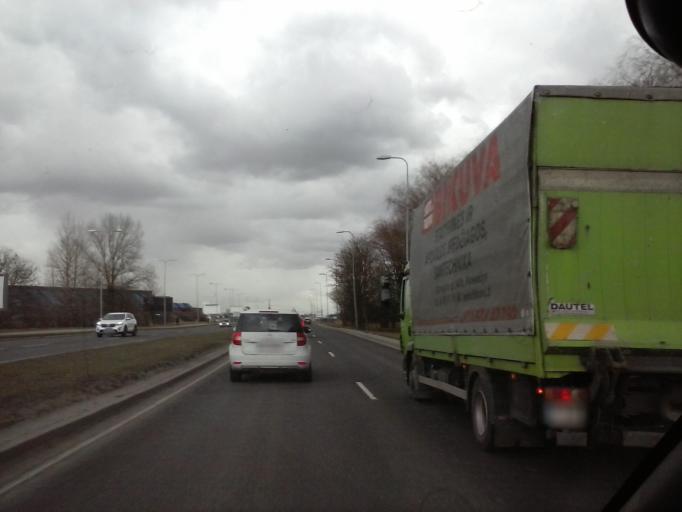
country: EE
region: Harju
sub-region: Tallinna linn
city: Tallinn
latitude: 59.4190
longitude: 24.7928
